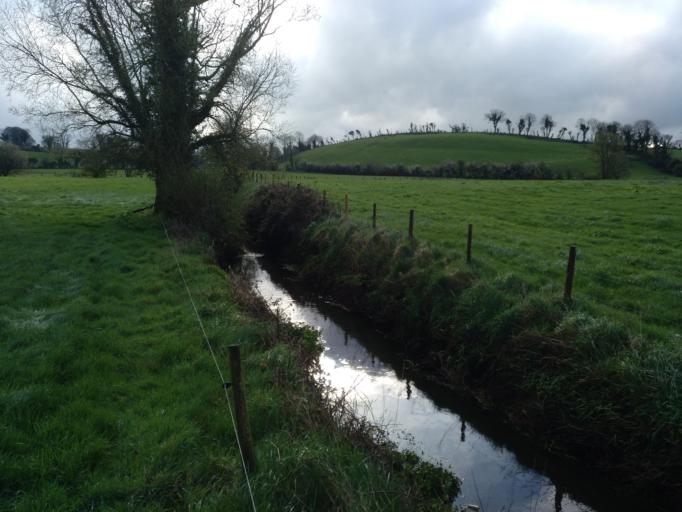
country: IE
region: Ulster
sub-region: County Monaghan
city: Clones
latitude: 54.1732
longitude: -7.2180
